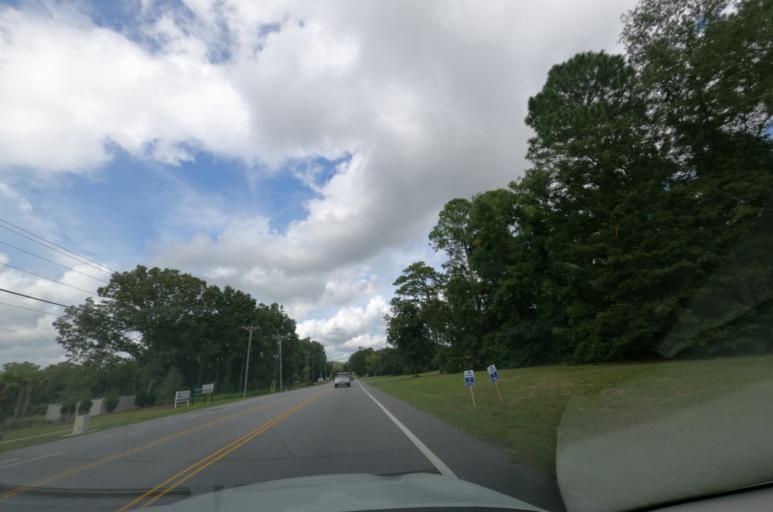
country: US
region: South Carolina
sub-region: Charleston County
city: Shell Point
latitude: 32.7353
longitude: -80.0538
